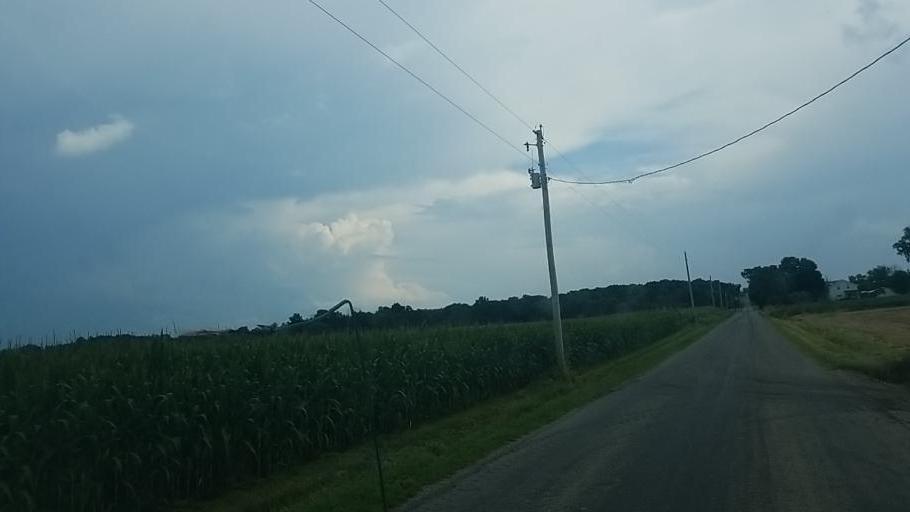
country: US
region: Ohio
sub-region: Wayne County
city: Creston
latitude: 40.9679
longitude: -81.9381
